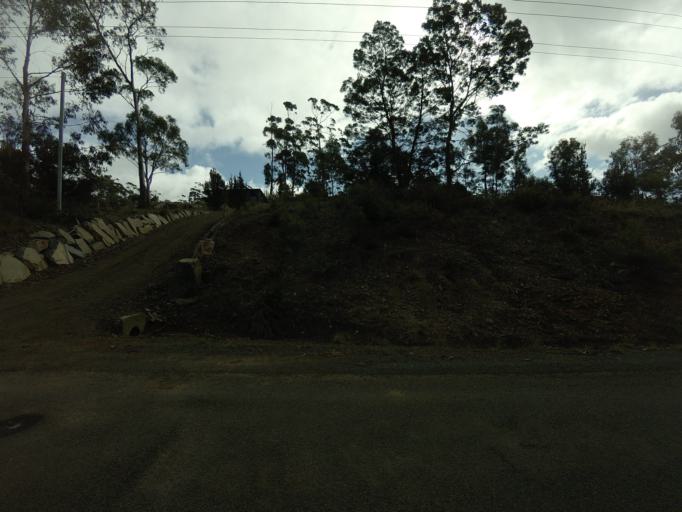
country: AU
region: Tasmania
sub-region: Sorell
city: Sorell
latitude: -42.5395
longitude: 147.9117
